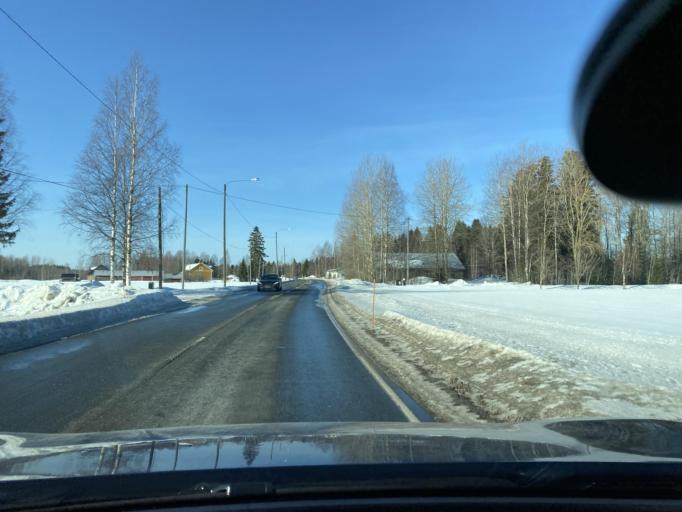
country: FI
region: Central Finland
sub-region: Joutsa
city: Joutsa
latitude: 61.8110
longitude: 25.9493
